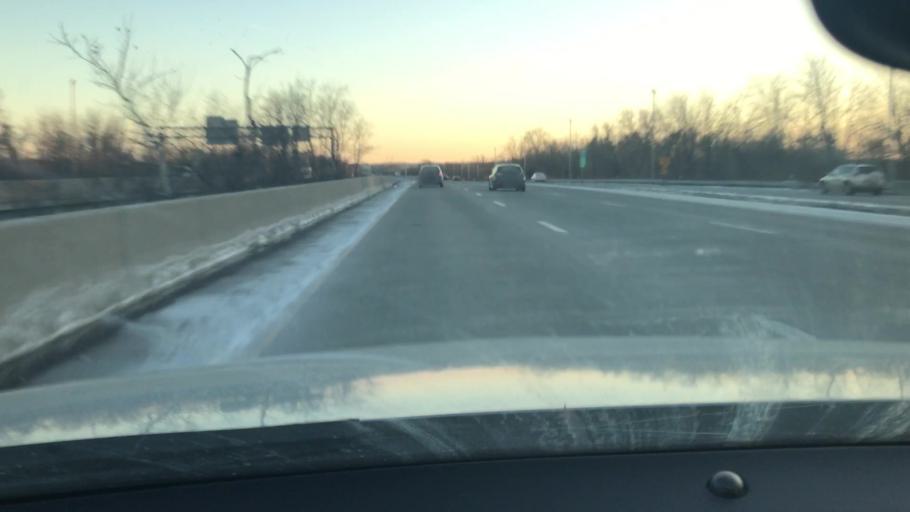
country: US
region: New Jersey
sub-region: Mercer County
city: White Horse
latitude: 40.1782
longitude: -74.7225
